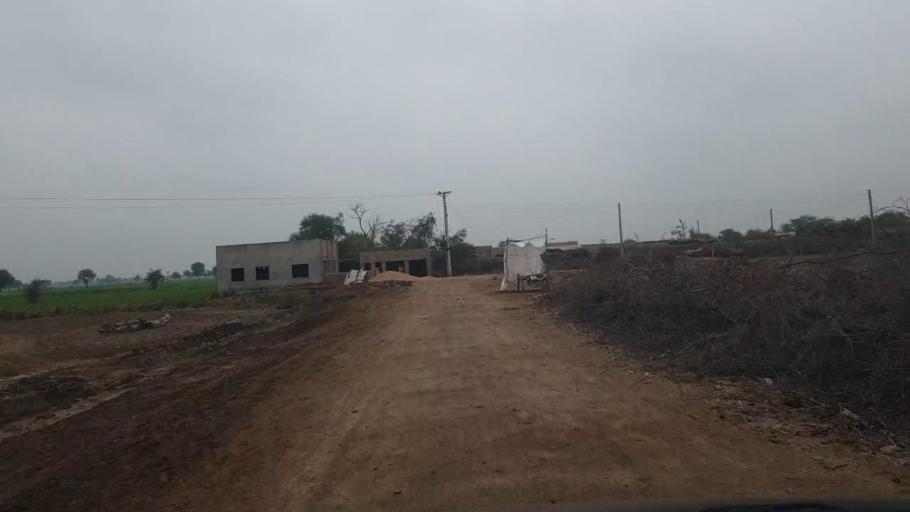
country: PK
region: Sindh
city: Tando Adam
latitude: 25.8516
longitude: 68.6947
